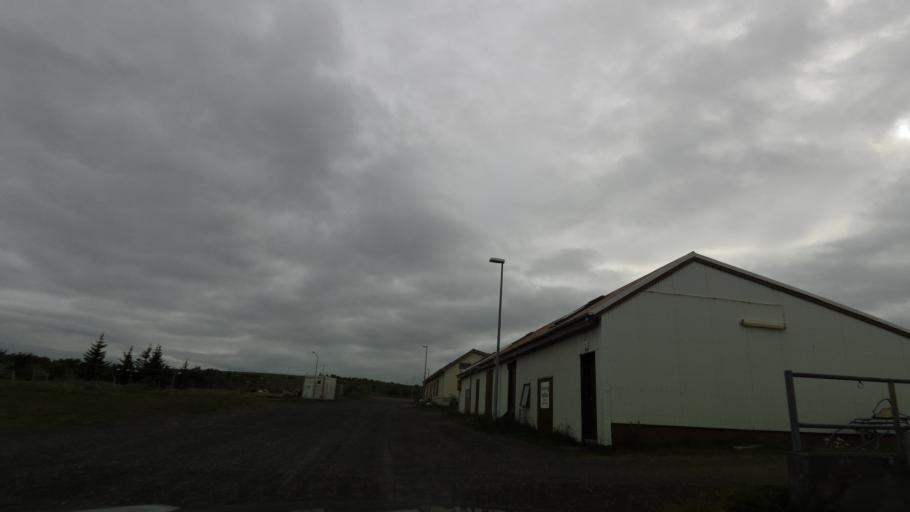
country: IS
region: Capital Region
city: Kopavogur
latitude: 64.0795
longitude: -21.8466
